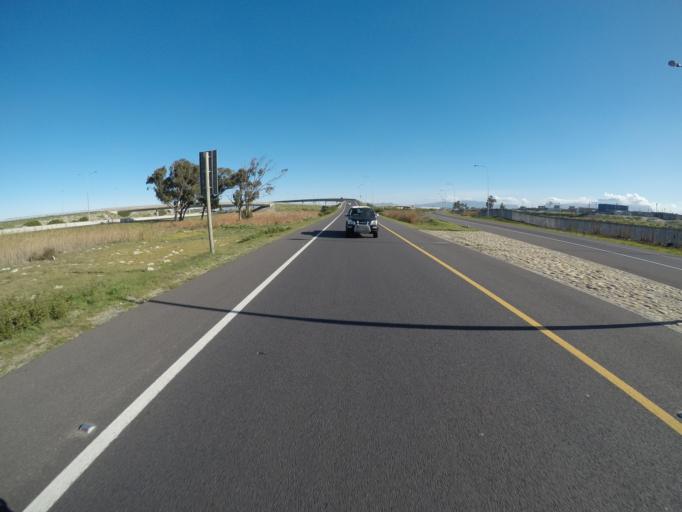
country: ZA
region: Western Cape
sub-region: City of Cape Town
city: Lansdowne
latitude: -33.9974
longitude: 18.6362
